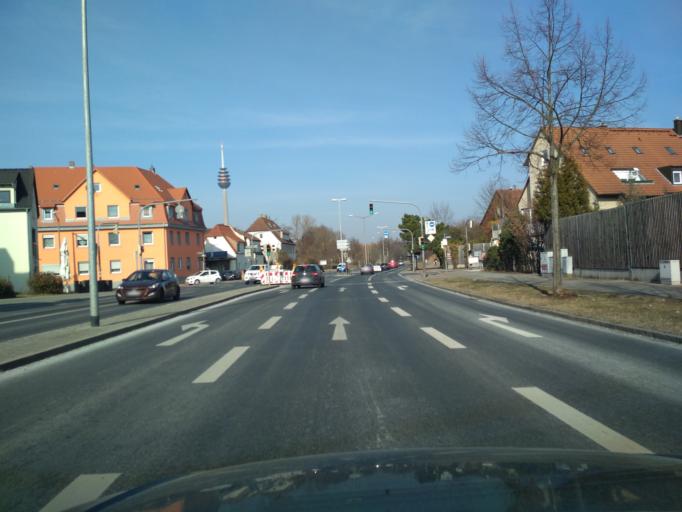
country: DE
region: Bavaria
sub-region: Regierungsbezirk Mittelfranken
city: Stein
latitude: 49.4131
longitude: 11.0344
